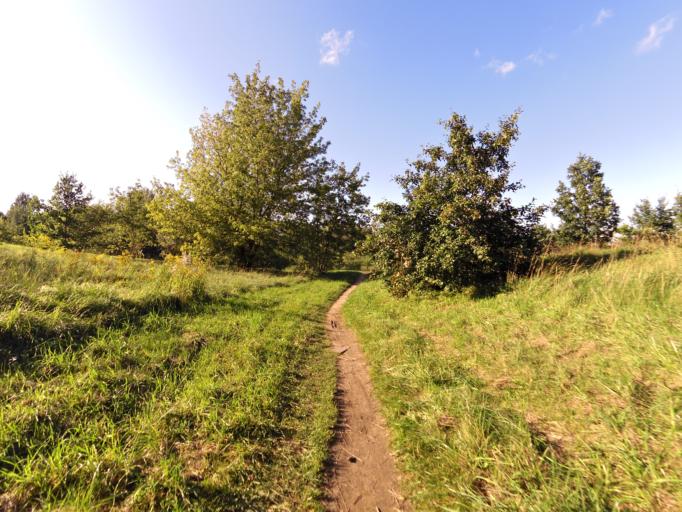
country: LT
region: Vilnius County
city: Seskine
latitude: 54.7134
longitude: 25.2627
